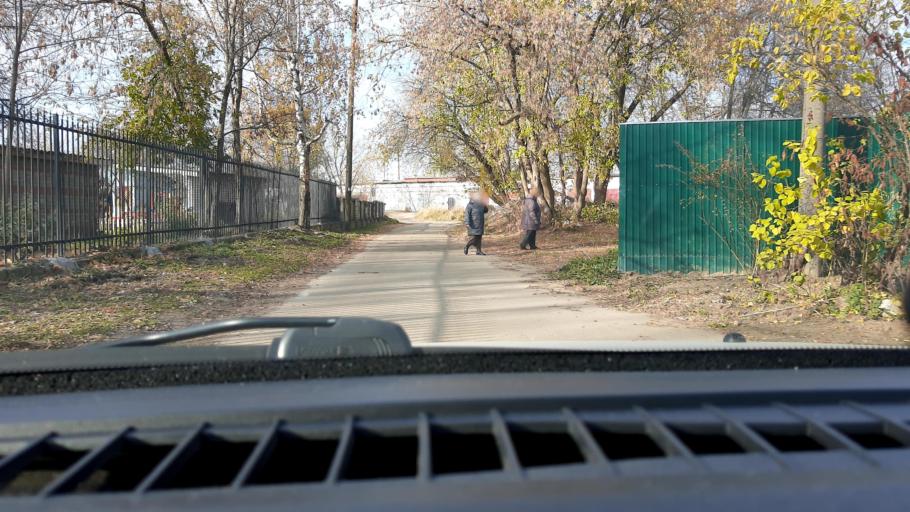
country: RU
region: Nizjnij Novgorod
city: Neklyudovo
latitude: 56.3539
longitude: 43.8500
